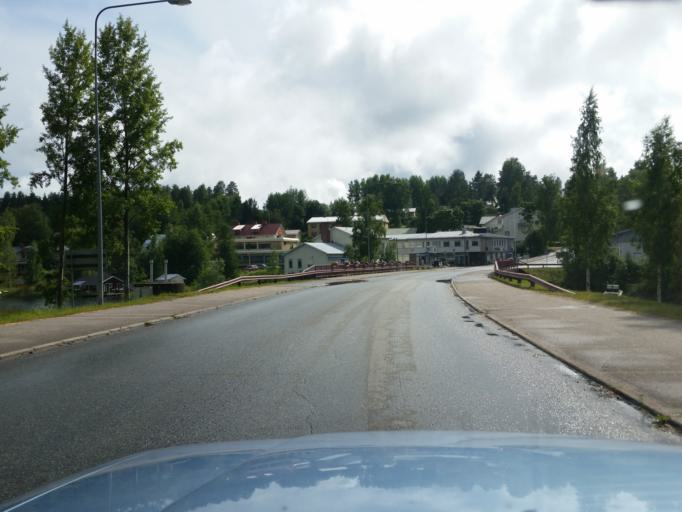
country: FI
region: Southern Savonia
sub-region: Savonlinna
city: Sulkava
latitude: 61.7879
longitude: 28.3742
